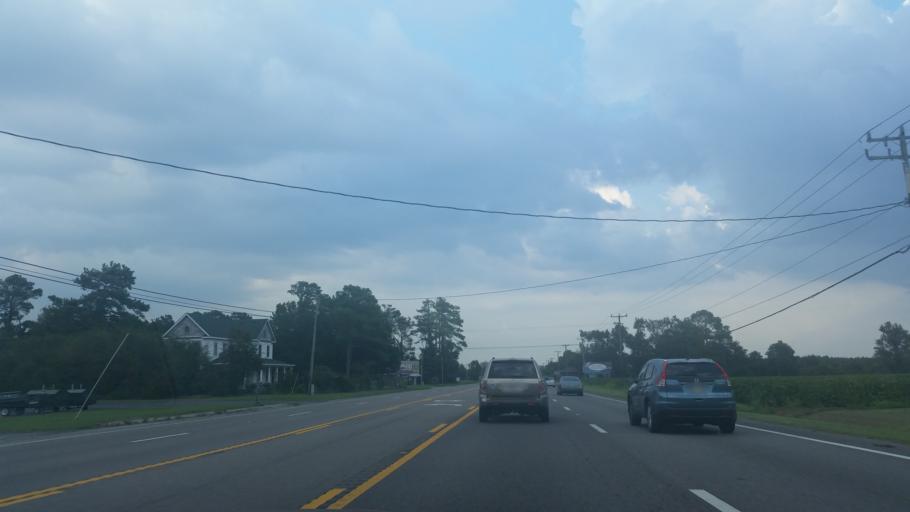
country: US
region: North Carolina
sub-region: Dare County
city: Southern Shores
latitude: 36.2028
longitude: -75.8654
